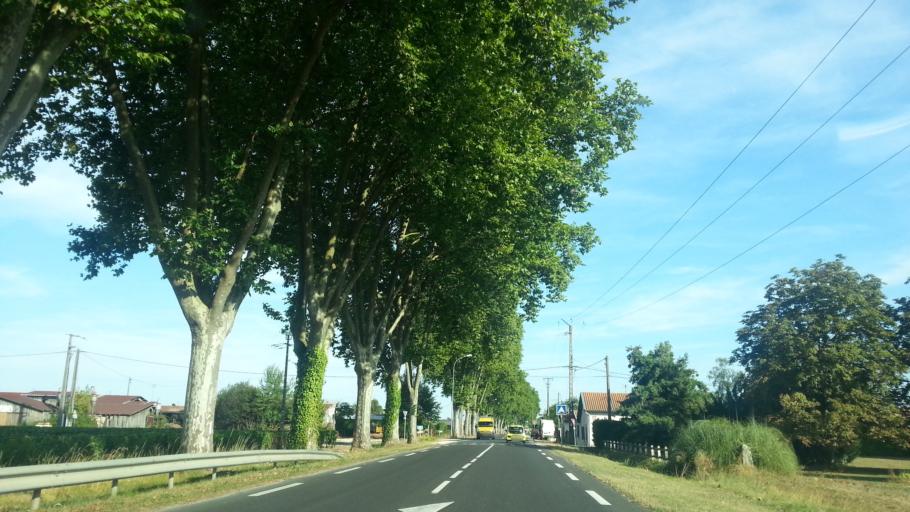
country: FR
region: Aquitaine
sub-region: Departement de la Gironde
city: Portets
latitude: 44.6788
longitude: -0.4038
